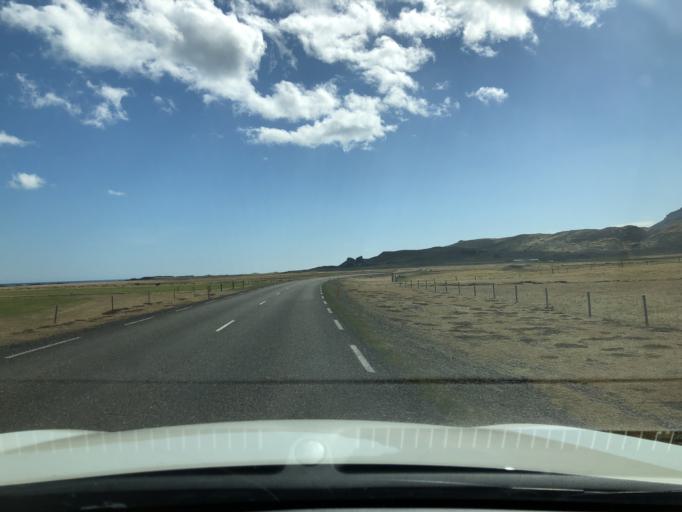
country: IS
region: East
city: Reydarfjoerdur
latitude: 64.5179
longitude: -14.5143
